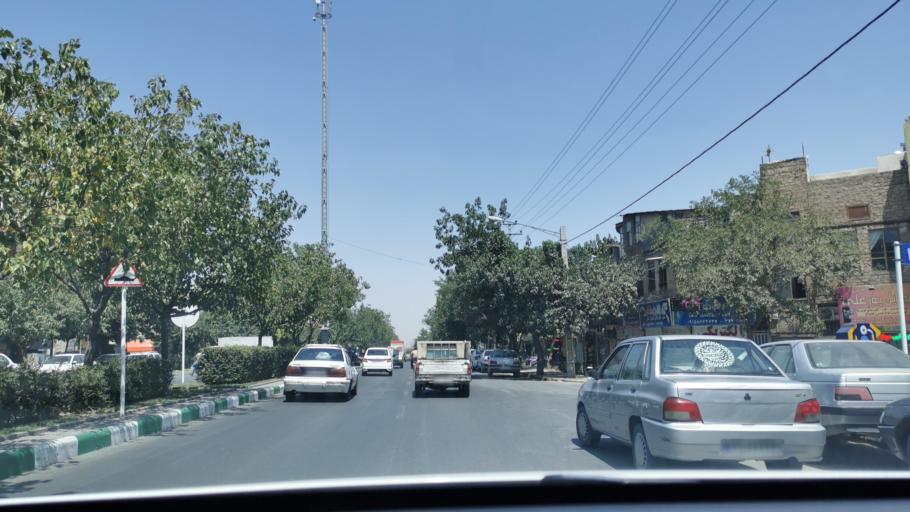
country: IR
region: Razavi Khorasan
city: Mashhad
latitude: 36.3428
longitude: 59.6256
